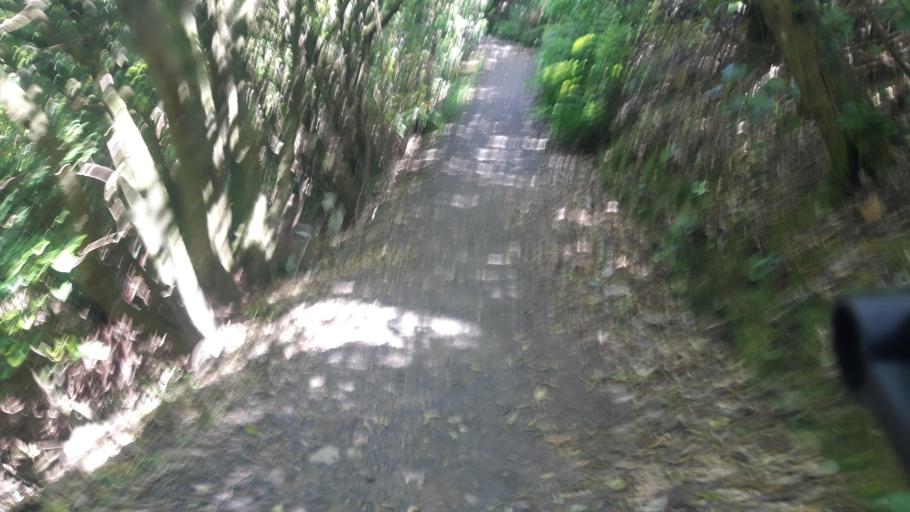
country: NZ
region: Marlborough
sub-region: Marlborough District
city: Picton
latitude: -41.2697
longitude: 174.0316
